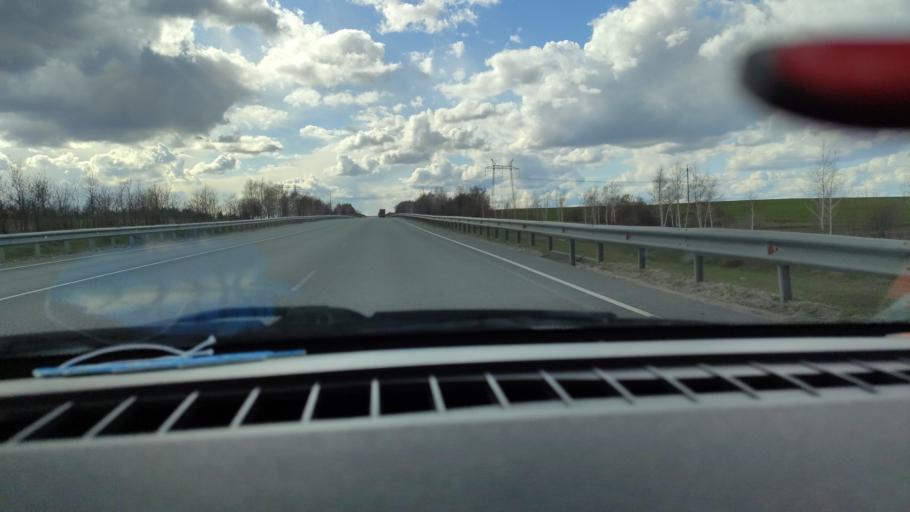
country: RU
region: Saratov
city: Tersa
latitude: 52.1010
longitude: 47.5107
